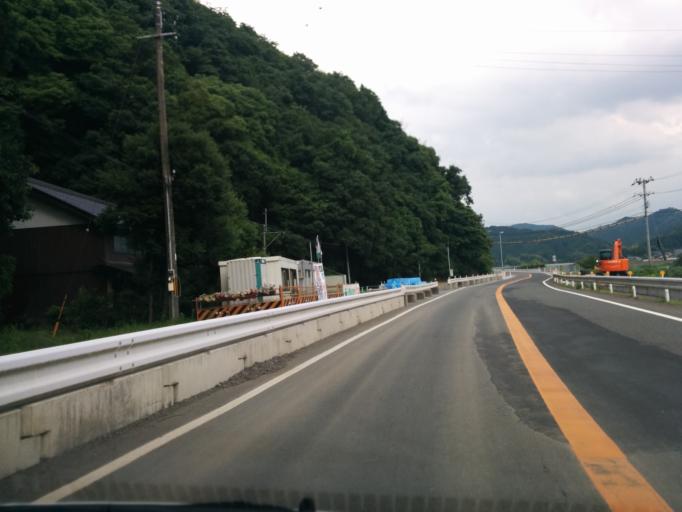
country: JP
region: Kyoto
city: Fukuchiyama
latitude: 35.3944
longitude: 135.1742
